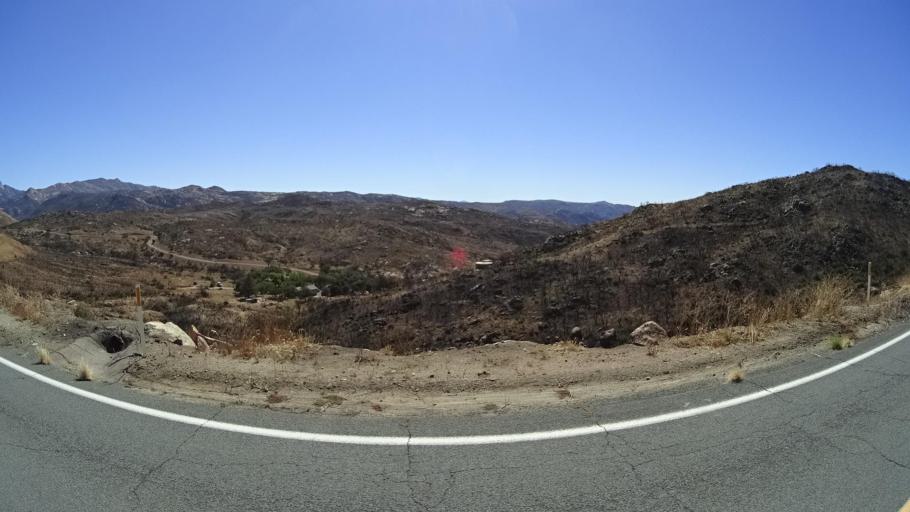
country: US
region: California
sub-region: San Diego County
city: Descanso
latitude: 32.7456
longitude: -116.6768
